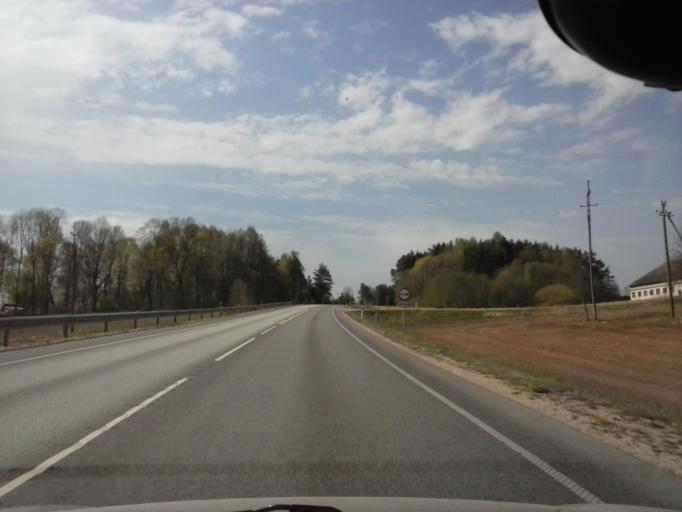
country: EE
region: Tartu
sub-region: UElenurme vald
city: Ulenurme
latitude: 58.2044
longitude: 26.7077
